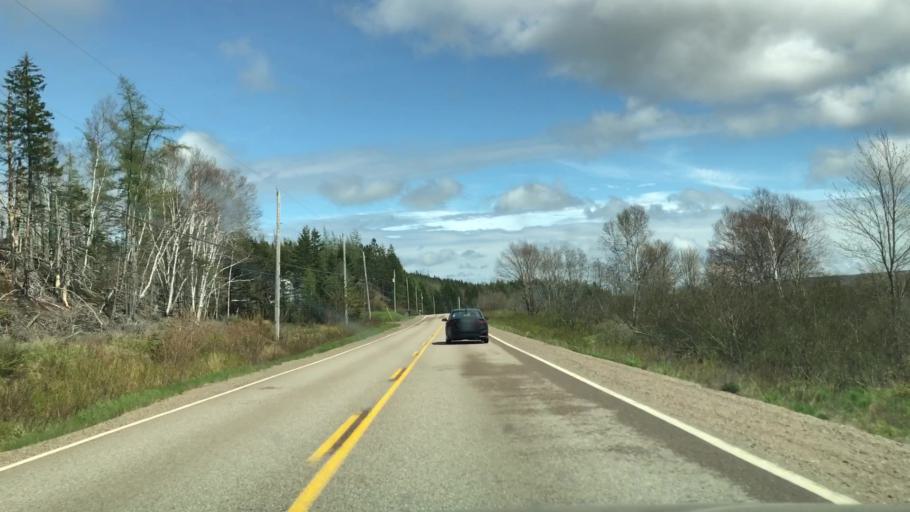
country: CA
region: Nova Scotia
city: Antigonish
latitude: 45.1927
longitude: -61.9946
